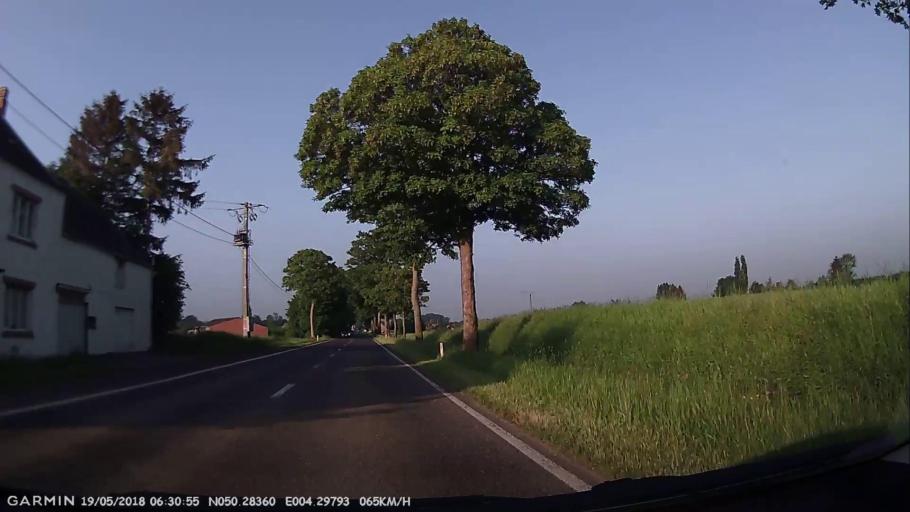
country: BE
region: Wallonia
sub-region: Province du Hainaut
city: Thuin
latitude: 50.2836
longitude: 4.2979
